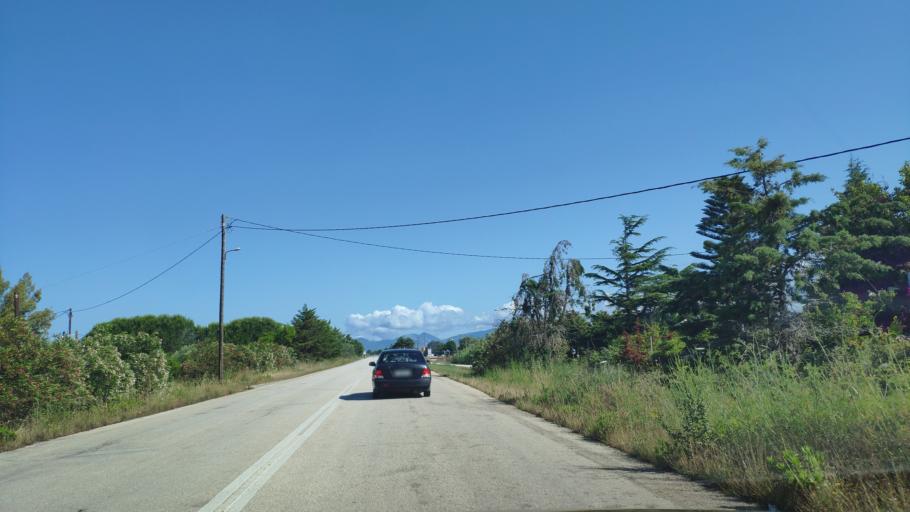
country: GR
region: Epirus
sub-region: Nomos Prevezis
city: Preveza
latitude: 38.9686
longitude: 20.7238
